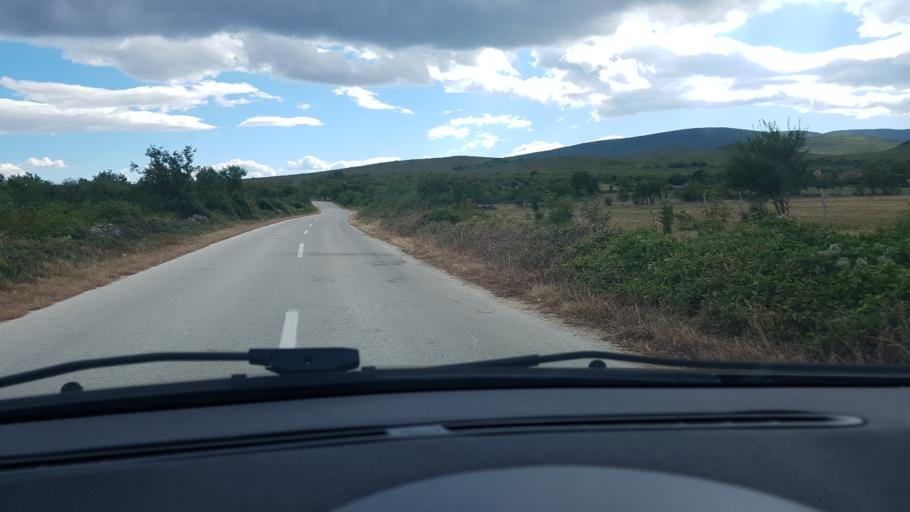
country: HR
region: Sibensko-Kniniska
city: Kistanje
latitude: 44.1019
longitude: 15.9394
